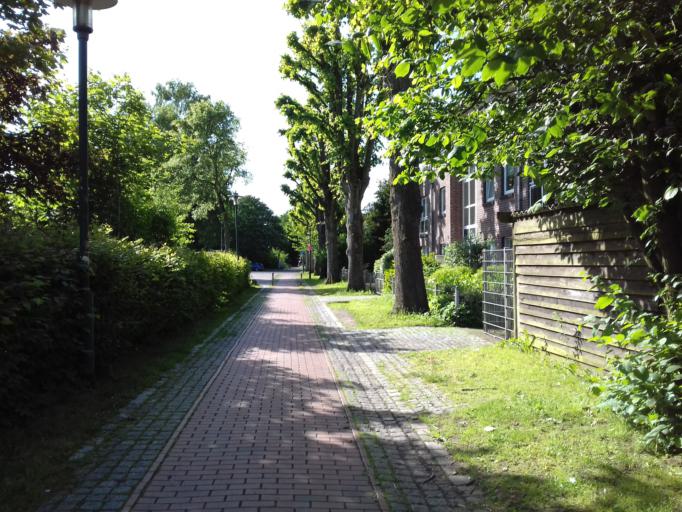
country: DE
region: Schleswig-Holstein
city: Neumunster
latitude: 54.0689
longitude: 9.9915
